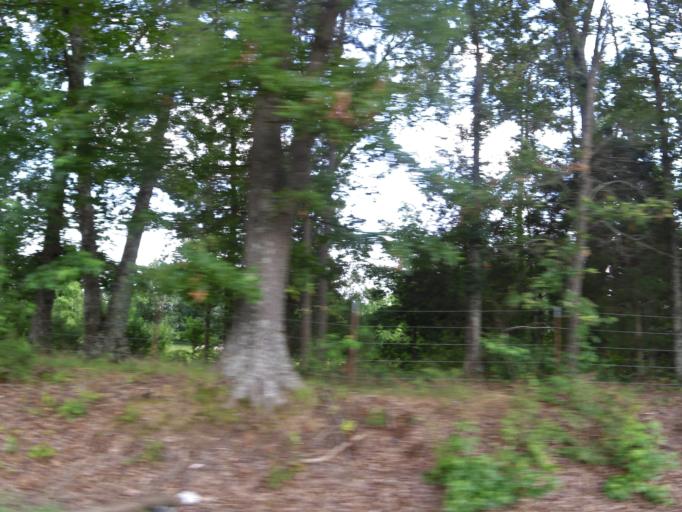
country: US
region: Tennessee
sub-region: Carroll County
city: Huntingdon
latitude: 35.9831
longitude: -88.5844
